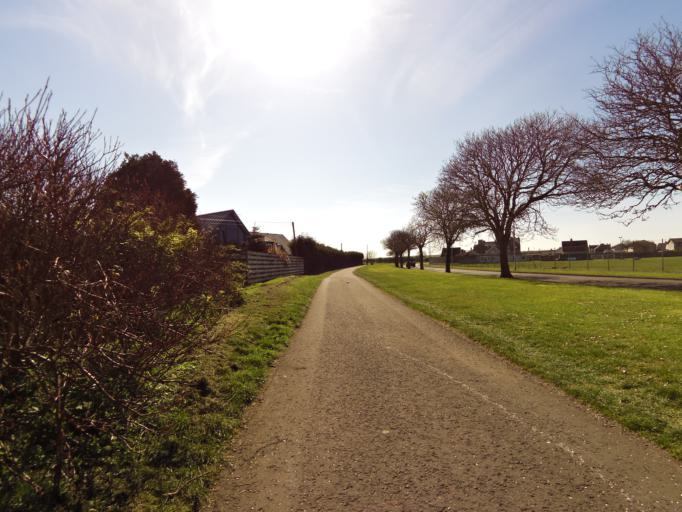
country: GB
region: Scotland
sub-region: Angus
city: Montrose
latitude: 56.7147
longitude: -2.4547
